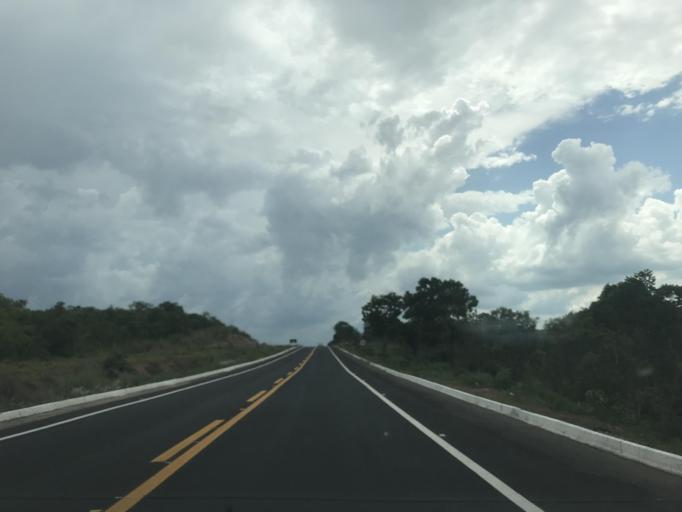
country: BR
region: Goias
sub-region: Caldas Novas
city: Caldas Novas
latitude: -17.7129
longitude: -48.7690
